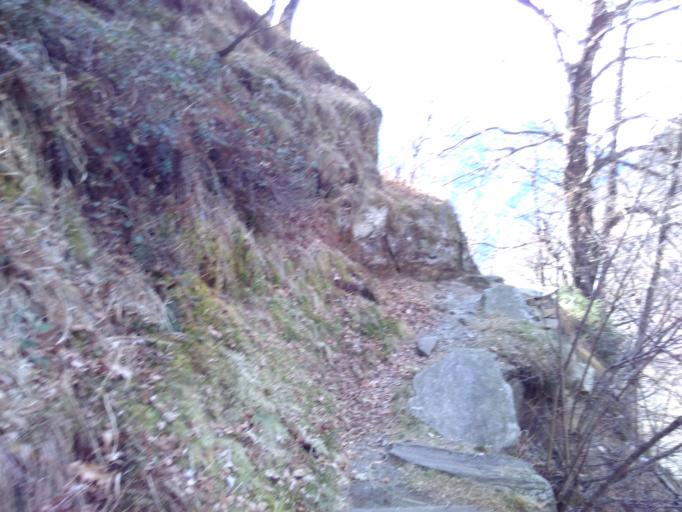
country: CH
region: Ticino
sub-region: Locarno District
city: Verscio
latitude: 46.2527
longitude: 8.7179
